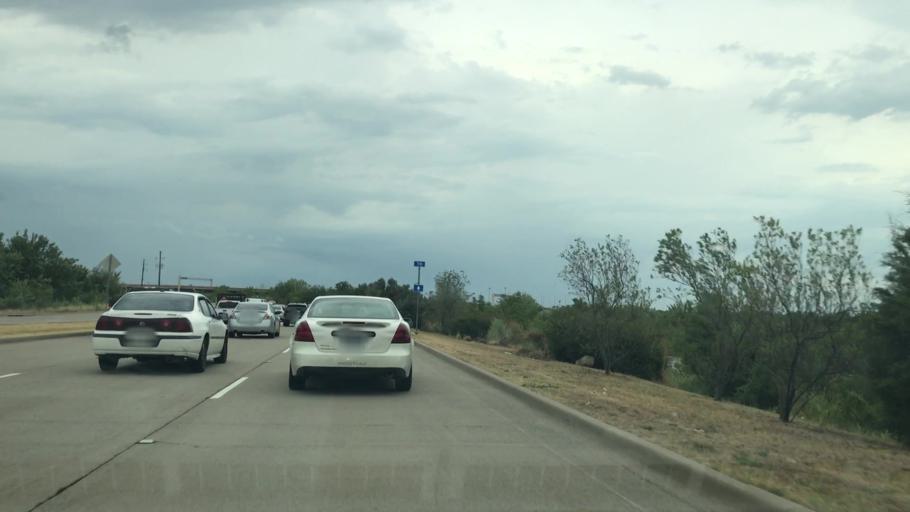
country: US
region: Texas
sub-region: Dallas County
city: Carrollton
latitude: 32.9616
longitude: -96.9233
